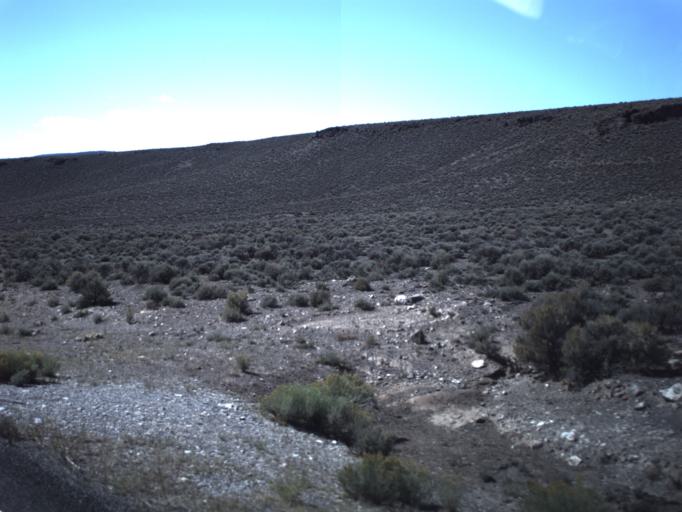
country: US
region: Utah
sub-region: Piute County
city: Junction
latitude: 38.1899
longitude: -112.0127
